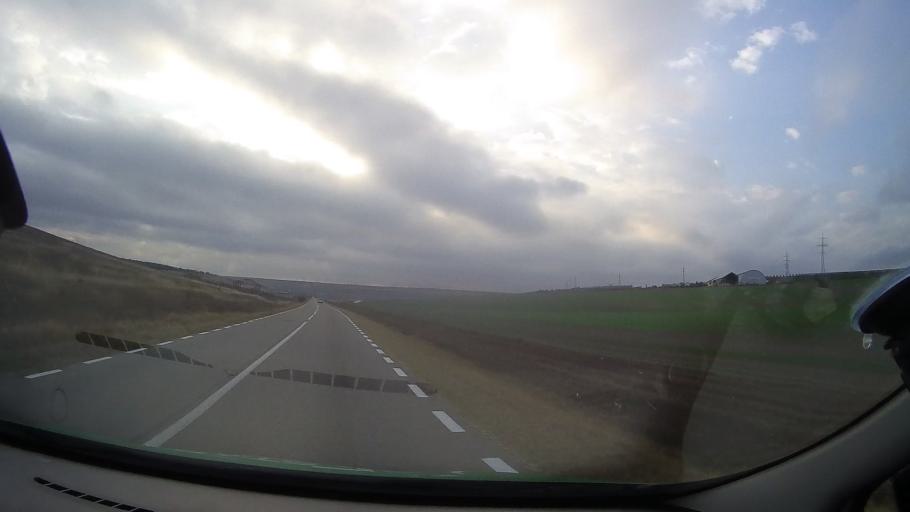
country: RO
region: Constanta
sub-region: Comuna Pestera
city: Pestera
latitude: 44.2006
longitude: 28.1393
